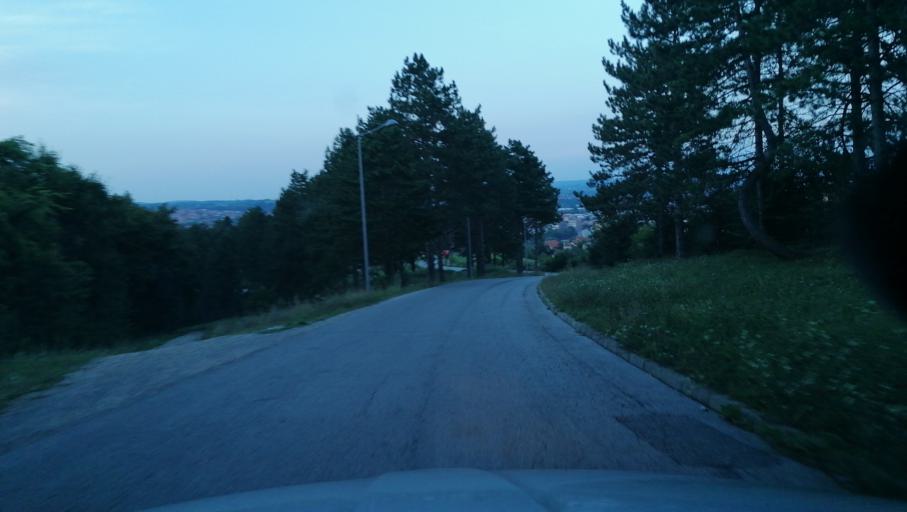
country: RS
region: Central Serbia
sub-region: Kolubarski Okrug
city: Valjevo
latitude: 44.2619
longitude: 19.8791
